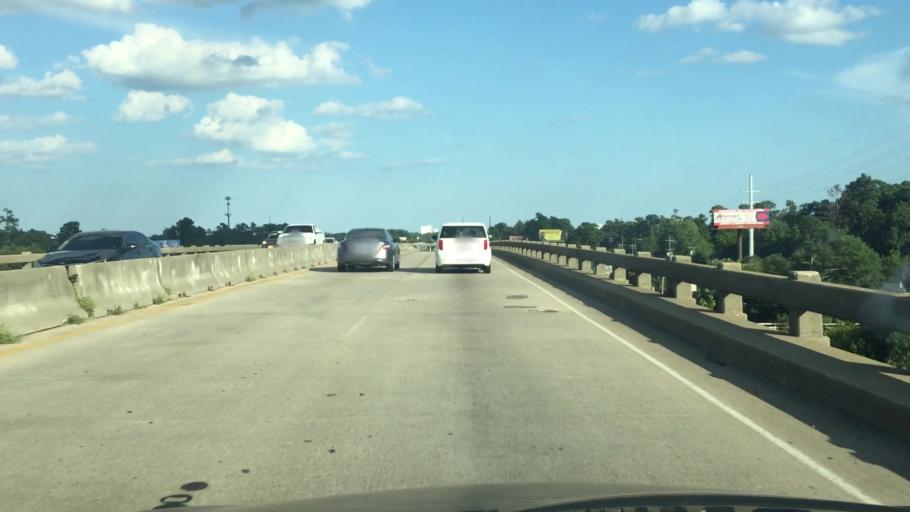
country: US
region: South Carolina
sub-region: Horry County
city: Forestbrook
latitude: 33.7144
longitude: -78.9223
